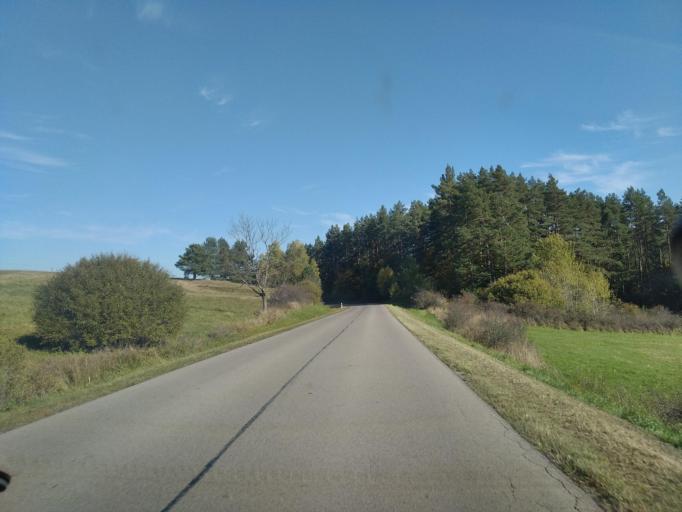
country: PL
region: Subcarpathian Voivodeship
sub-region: Powiat sanocki
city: Bukowsko
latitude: 49.4131
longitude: 21.9512
